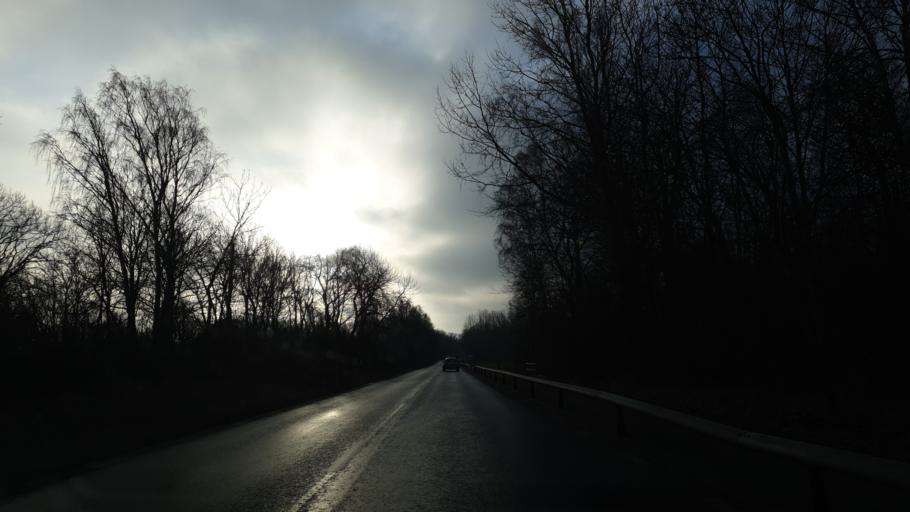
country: SE
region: Blekinge
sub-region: Karlshamns Kommun
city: Morrum
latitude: 56.1356
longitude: 14.6718
